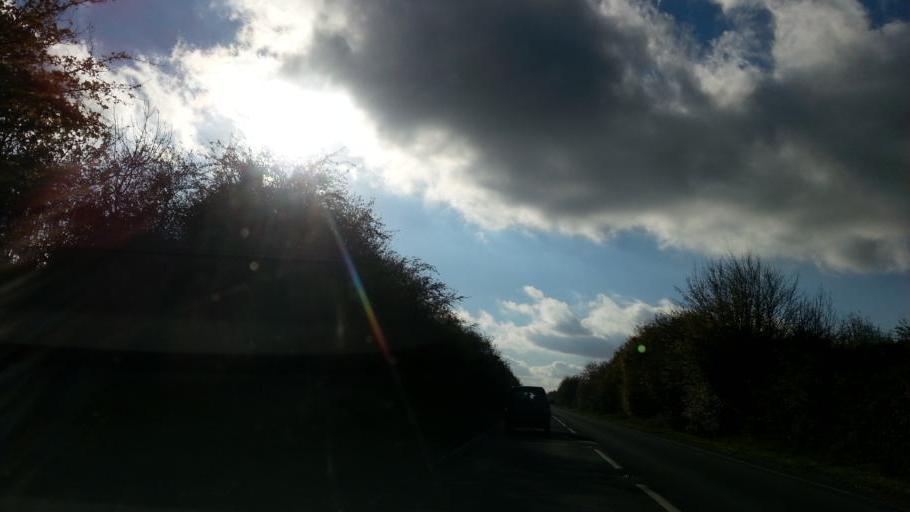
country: GB
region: England
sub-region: Norfolk
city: Harleston
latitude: 52.3910
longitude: 1.2741
